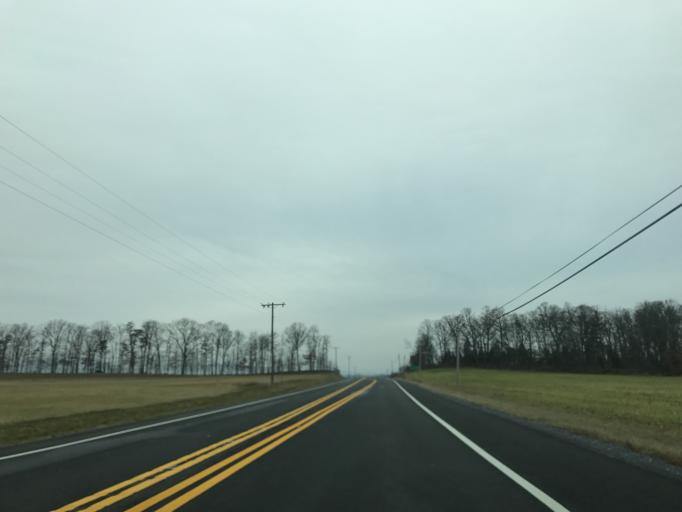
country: US
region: Maryland
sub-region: Frederick County
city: Emmitsburg
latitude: 39.6938
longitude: -77.2812
